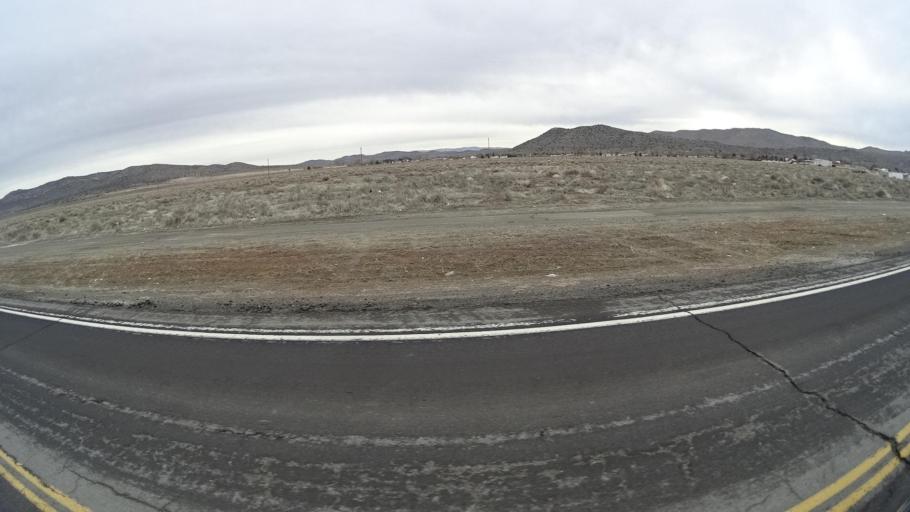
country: US
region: Nevada
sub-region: Washoe County
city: Lemmon Valley
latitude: 39.6665
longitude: -119.8307
